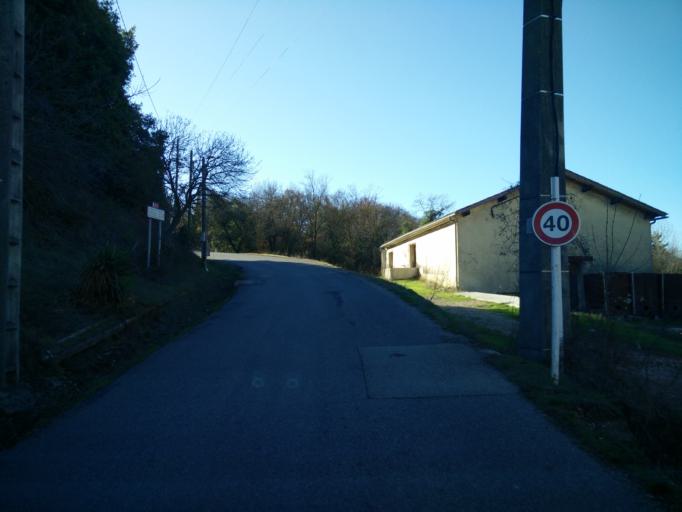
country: FR
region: Provence-Alpes-Cote d'Azur
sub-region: Departement du Var
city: Gonfaron
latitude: 43.3179
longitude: 6.2899
